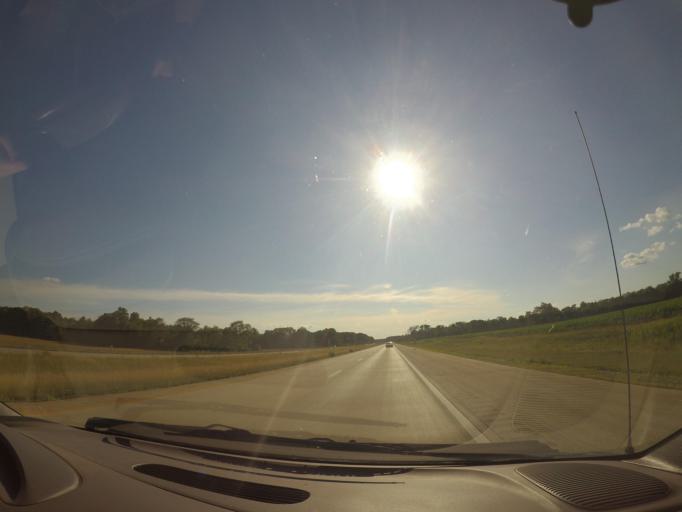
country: US
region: Ohio
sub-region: Henry County
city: Liberty Center
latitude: 41.4332
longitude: -83.9488
